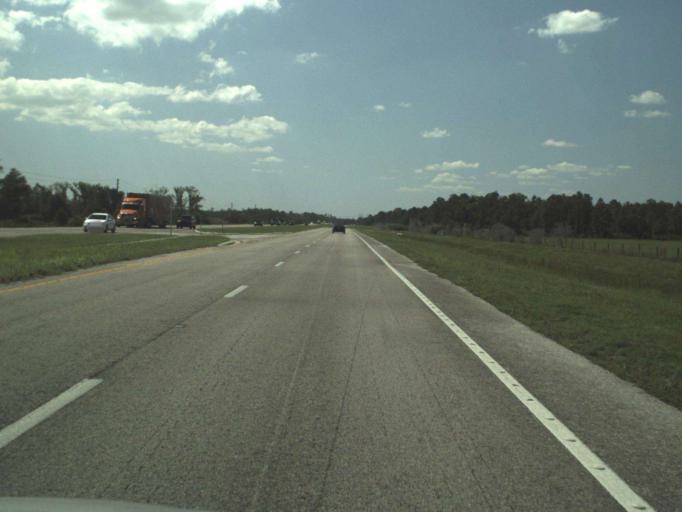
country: US
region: Florida
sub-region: Orange County
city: Wedgefield
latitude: 28.4794
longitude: -81.0254
